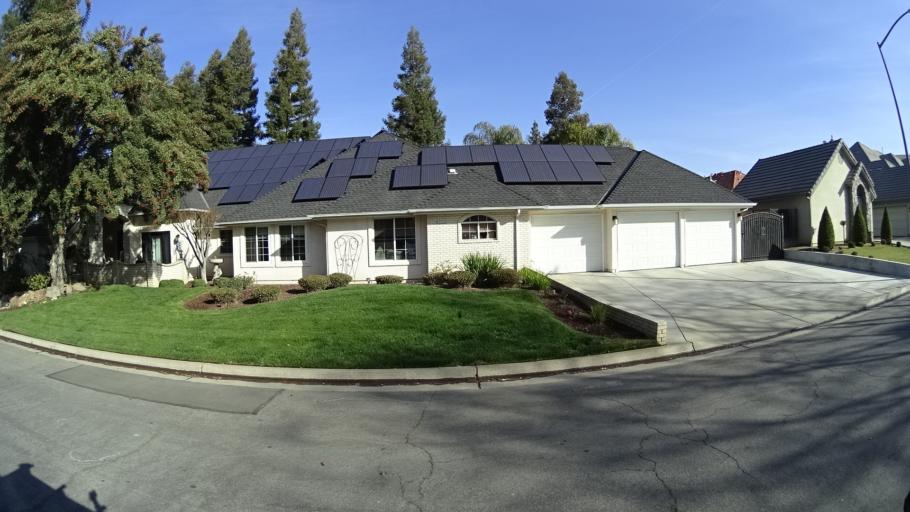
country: US
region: California
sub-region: Fresno County
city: Clovis
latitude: 36.8817
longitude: -119.7637
